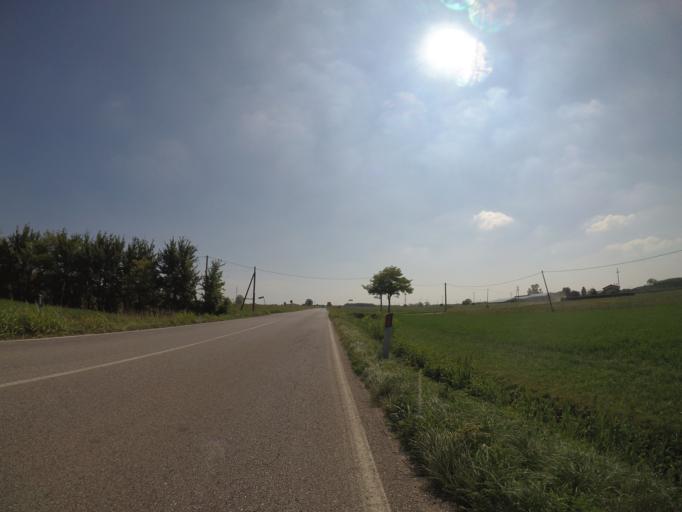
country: IT
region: Friuli Venezia Giulia
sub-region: Provincia di Udine
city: Pocenia
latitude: 45.8220
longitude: 13.1010
